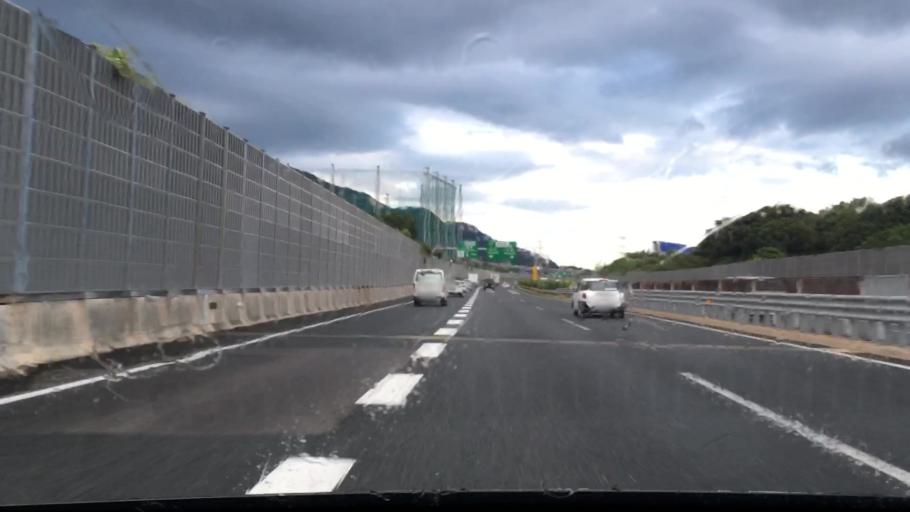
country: JP
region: Fukuoka
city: Kitakyushu
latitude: 33.8276
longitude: 130.8986
